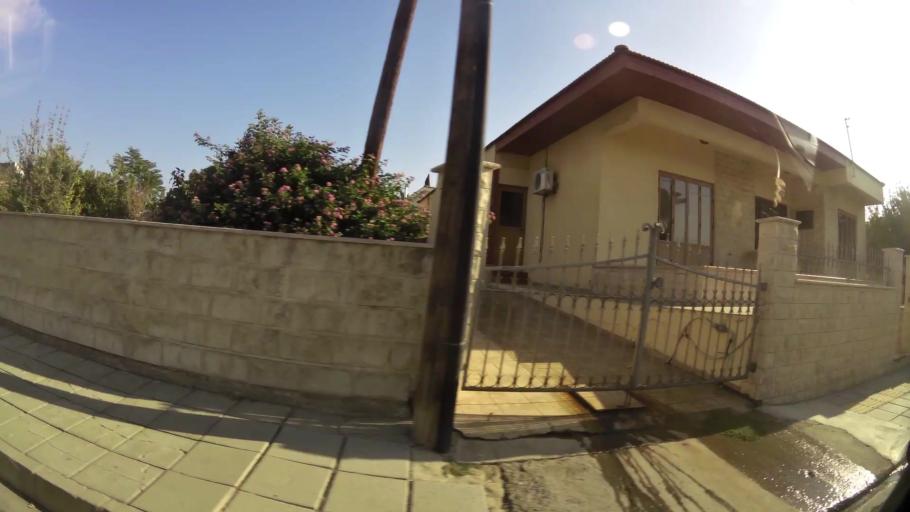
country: CY
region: Larnaka
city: Aradippou
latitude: 34.9461
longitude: 33.5940
